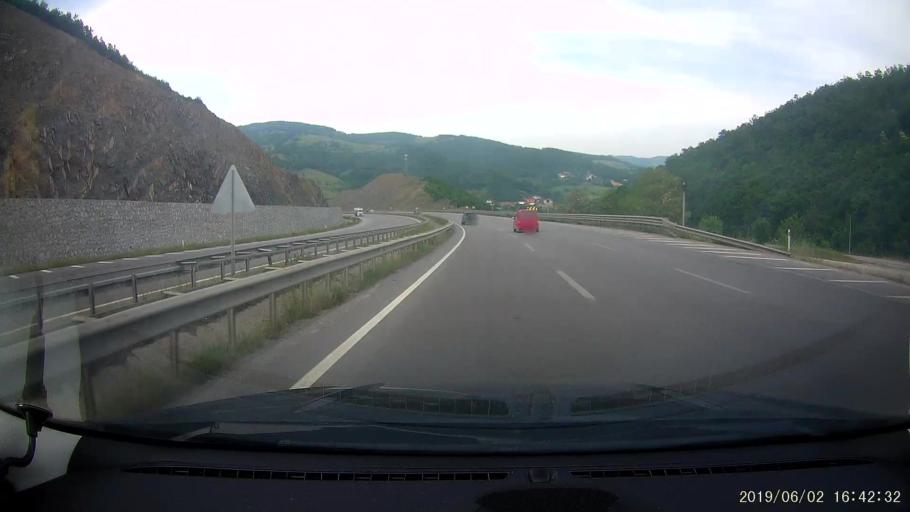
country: TR
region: Samsun
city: Kavak
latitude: 41.1198
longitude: 36.1345
